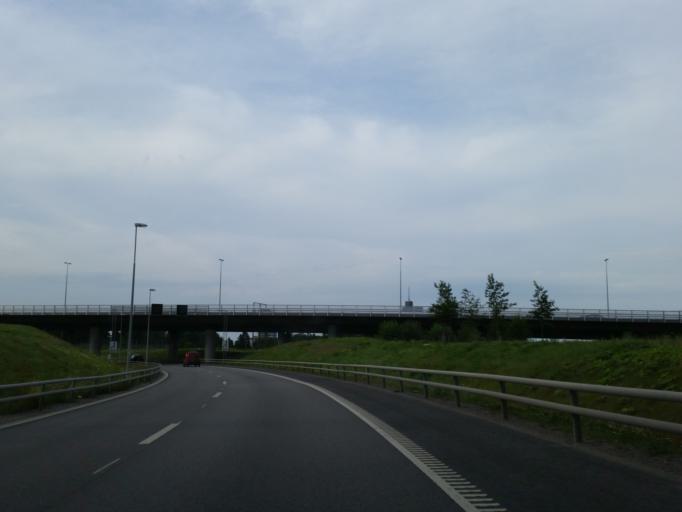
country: SE
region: Stockholm
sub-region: Stockholms Kommun
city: Kista
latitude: 59.3880
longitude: 17.9402
